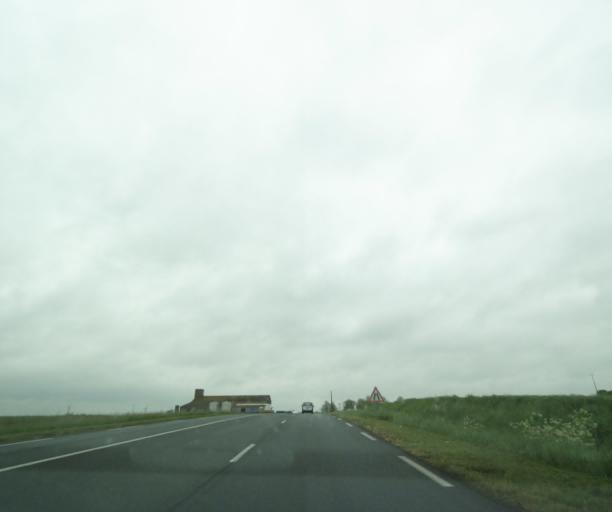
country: FR
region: Poitou-Charentes
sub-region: Departement de la Charente-Maritime
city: Pons
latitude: 45.6446
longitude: -0.5807
